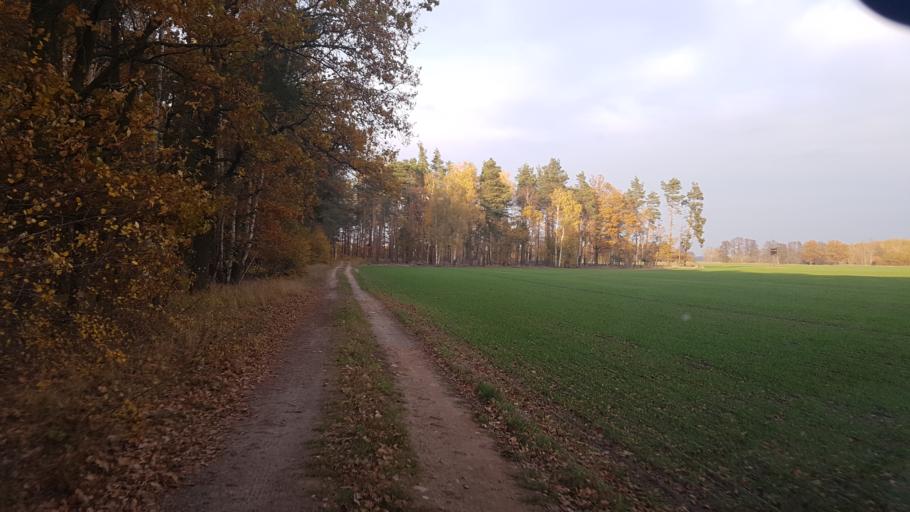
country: DE
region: Brandenburg
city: Schonewalde
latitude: 51.6404
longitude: 13.5998
